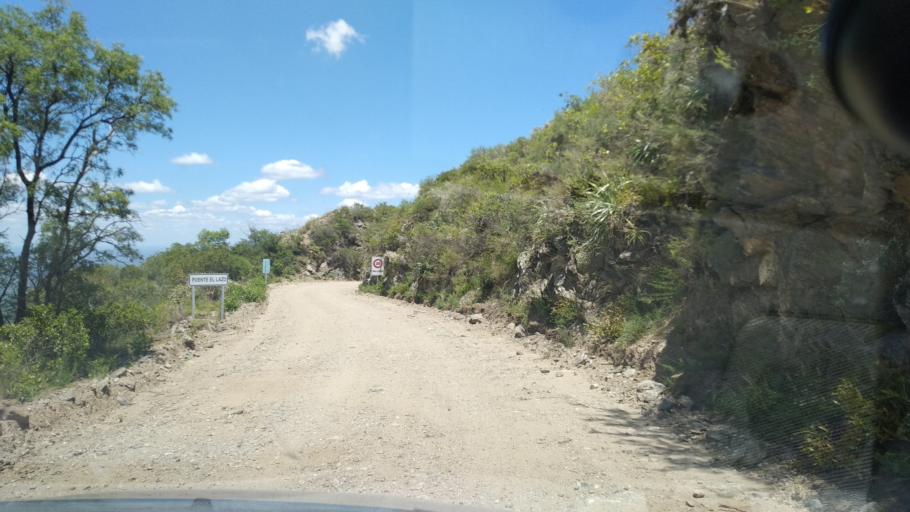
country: AR
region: Cordoba
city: Salsacate
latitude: -31.3771
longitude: -65.4020
